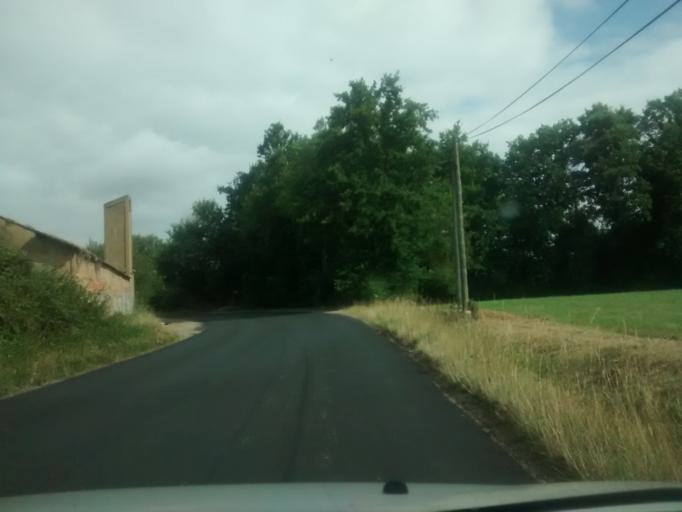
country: FR
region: Brittany
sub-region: Departement d'Ille-et-Vilaine
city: Saint-Jacques-de-la-Lande
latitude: 48.0847
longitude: -1.7314
